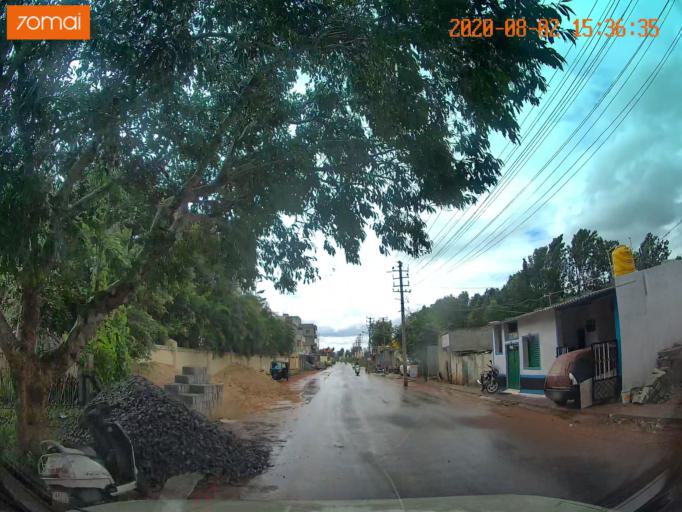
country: IN
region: Karnataka
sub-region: Bangalore Urban
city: Anekal
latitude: 12.8280
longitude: 77.6492
